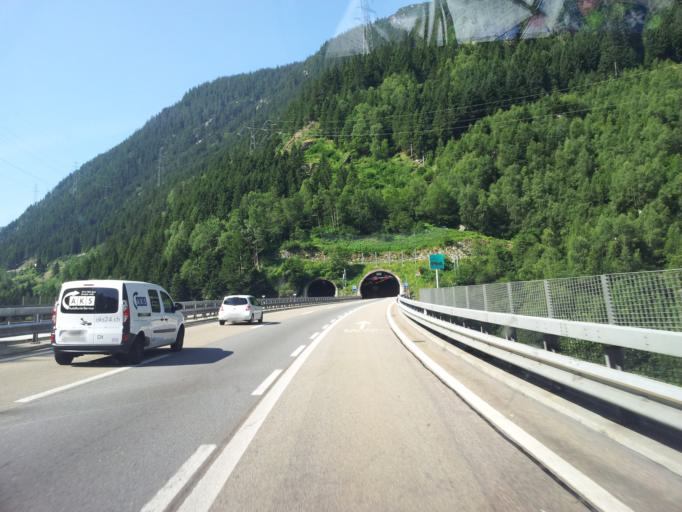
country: CH
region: Uri
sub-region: Uri
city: Andermatt
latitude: 46.6879
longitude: 8.5938
